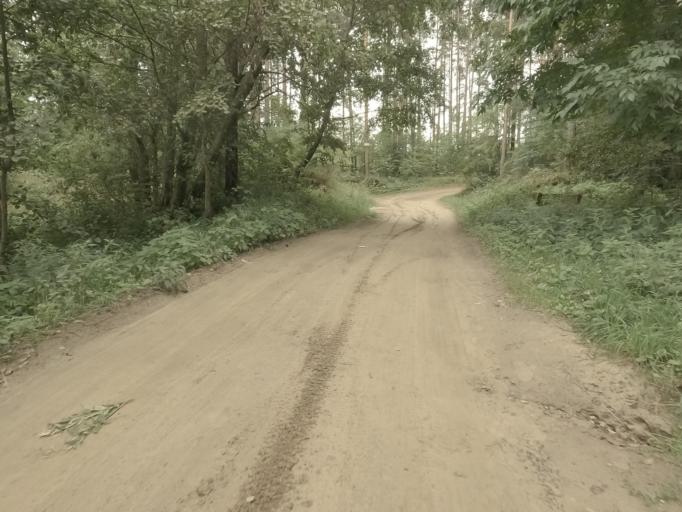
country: RU
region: Leningrad
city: Kirovsk
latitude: 59.8977
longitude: 31.0061
